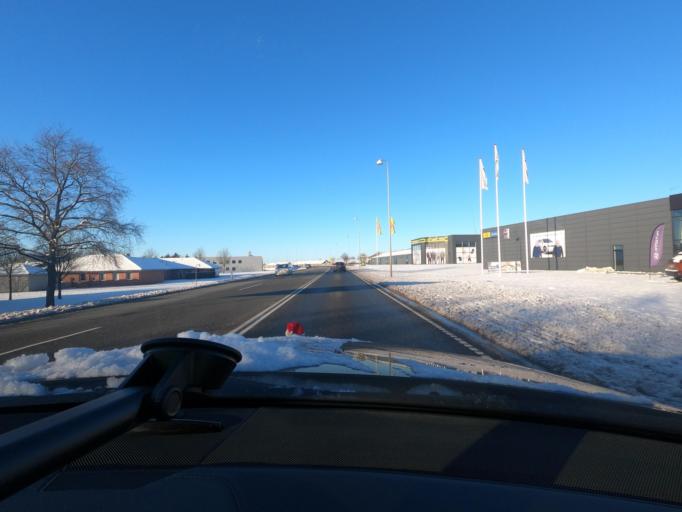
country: DK
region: South Denmark
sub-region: Aabenraa Kommune
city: Rodekro
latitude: 55.0683
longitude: 9.3588
